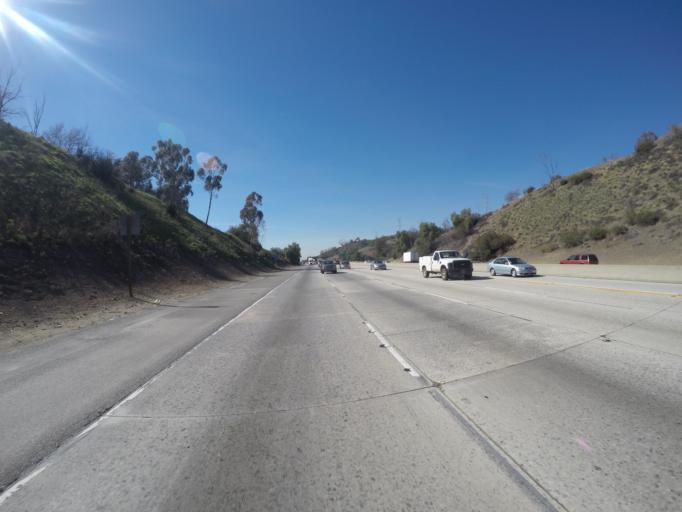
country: US
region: California
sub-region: Los Angeles County
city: Charter Oak
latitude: 34.1175
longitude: -117.8499
